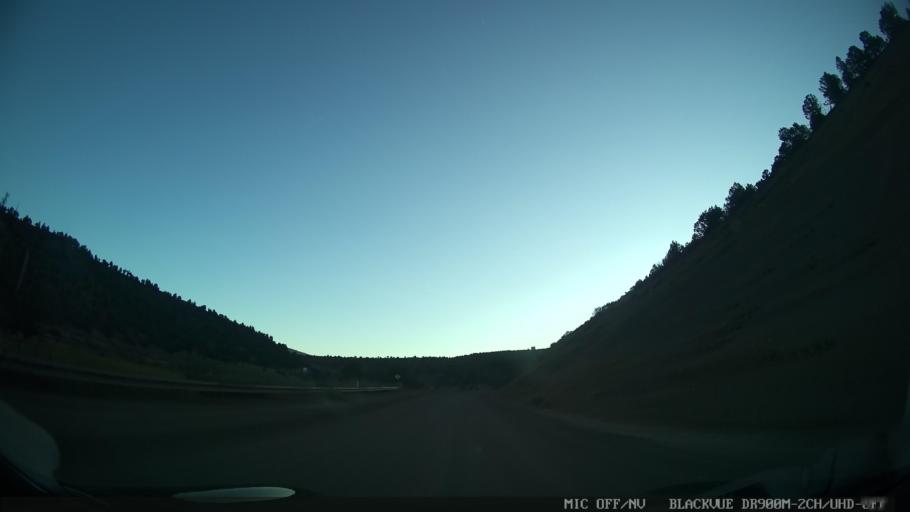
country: US
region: Colorado
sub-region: Eagle County
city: Edwards
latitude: 39.8906
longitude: -106.6168
